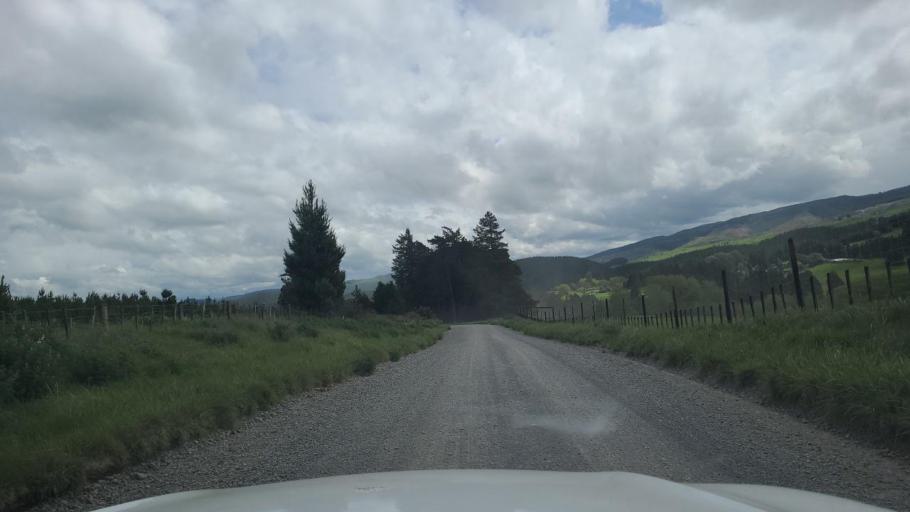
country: NZ
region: Hawke's Bay
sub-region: Napier City
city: Taradale
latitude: -39.2714
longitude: 176.6902
